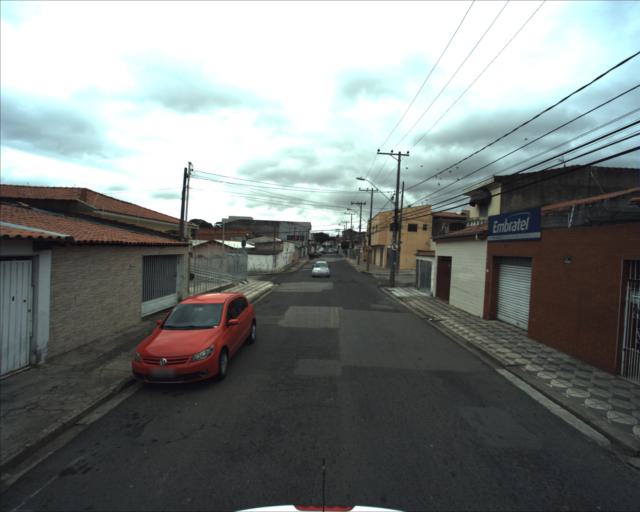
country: BR
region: Sao Paulo
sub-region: Sorocaba
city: Sorocaba
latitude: -23.4807
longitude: -47.4673
